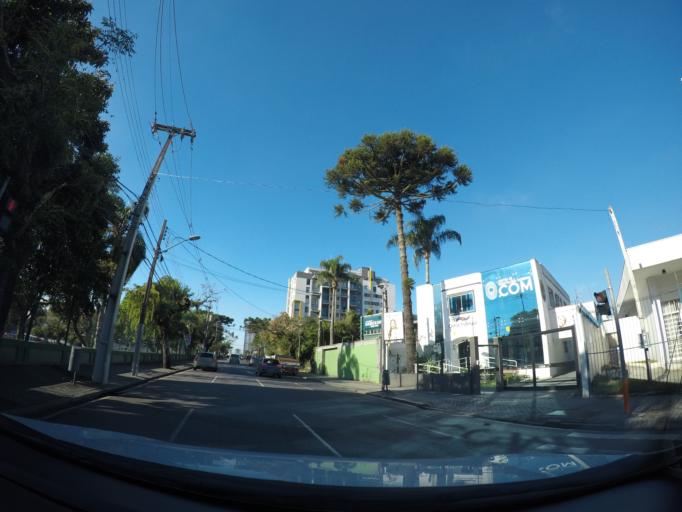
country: BR
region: Parana
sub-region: Curitiba
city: Curitiba
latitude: -25.4213
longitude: -49.2613
